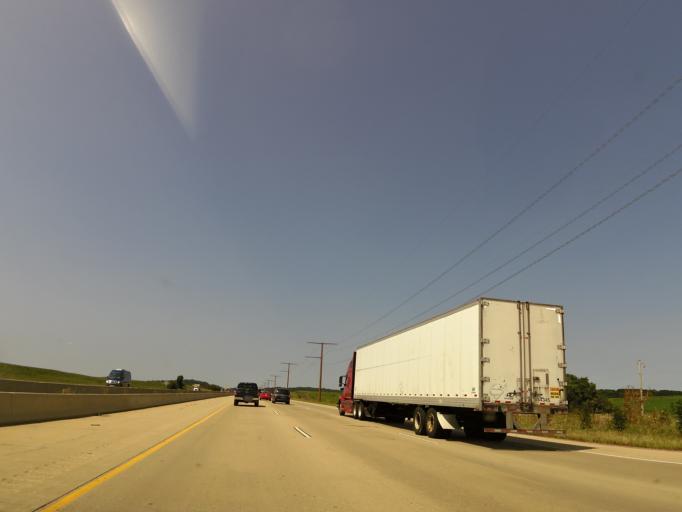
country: US
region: Wisconsin
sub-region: Dane County
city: De Forest
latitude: 43.2981
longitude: -89.4218
